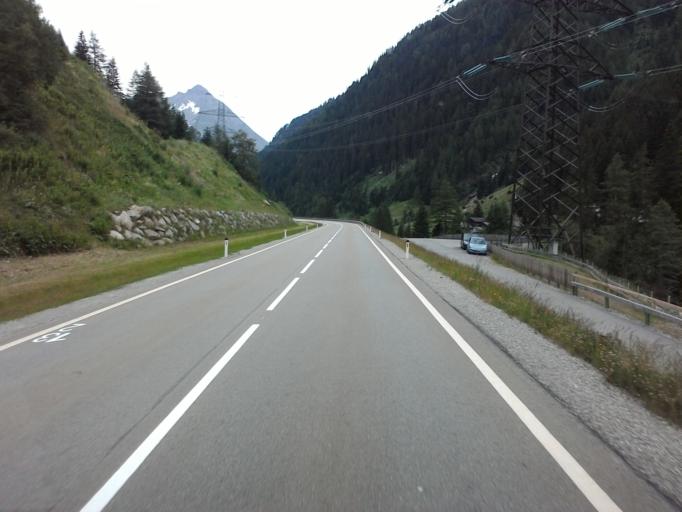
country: AT
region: Tyrol
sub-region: Politischer Bezirk Lienz
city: Matrei in Osttirol
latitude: 47.1064
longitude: 12.5057
